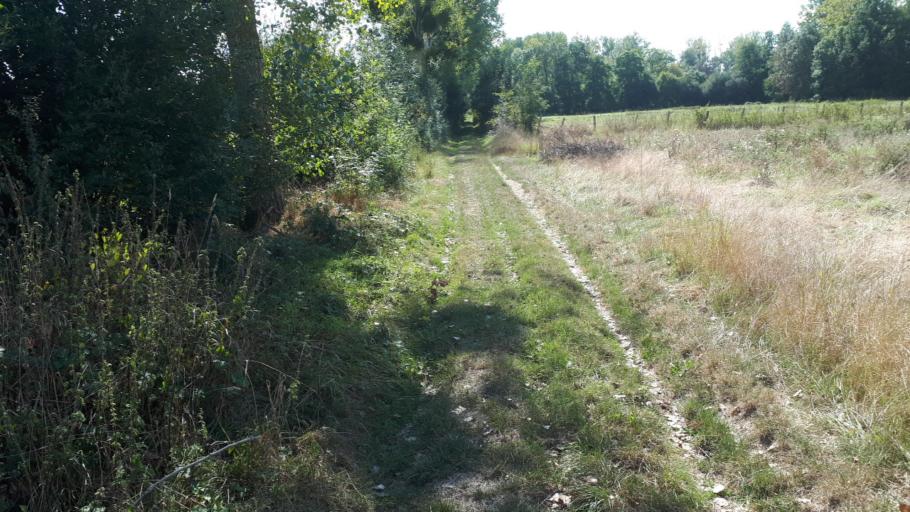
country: FR
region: Centre
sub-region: Departement du Loir-et-Cher
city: Villiers-sur-Loir
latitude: 47.8166
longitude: 0.9602
